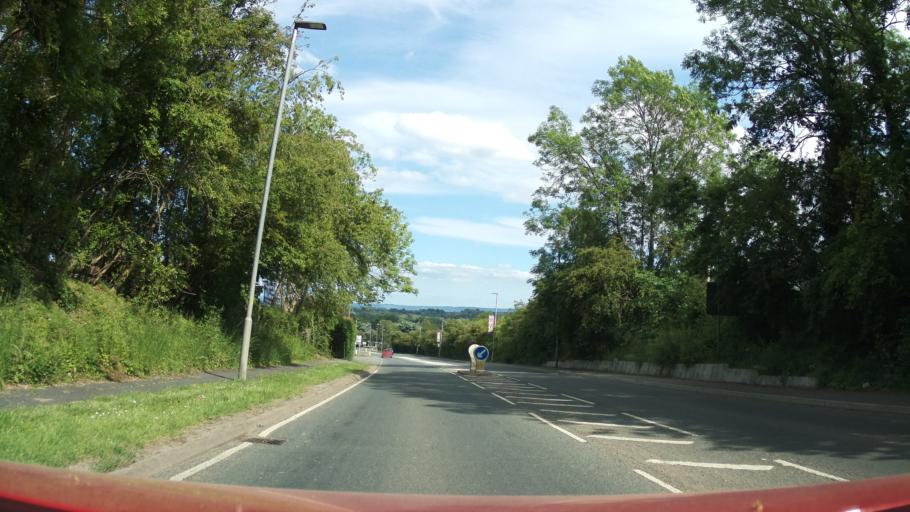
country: GB
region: England
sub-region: Worcestershire
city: Pershore
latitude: 52.1150
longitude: -2.0885
